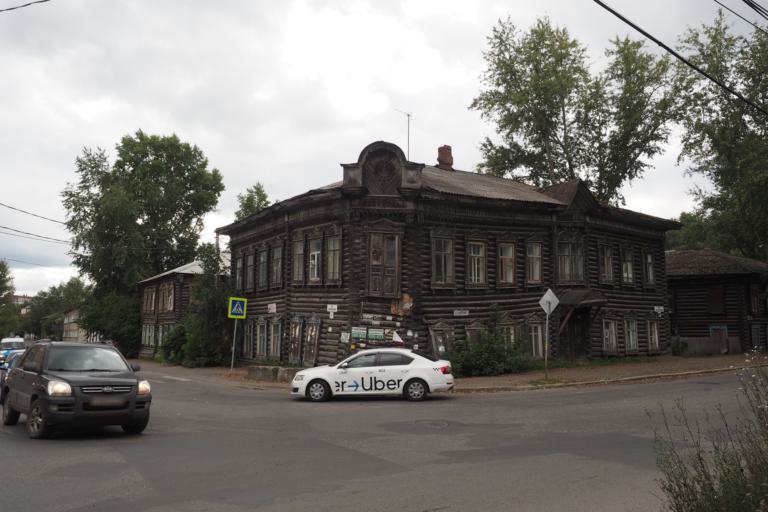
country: RU
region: Tomsk
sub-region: Tomskiy Rayon
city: Tomsk
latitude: 56.4847
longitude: 84.9576
